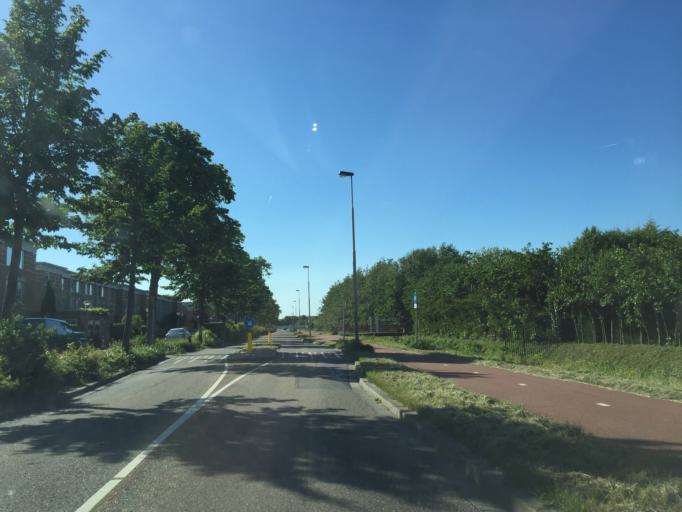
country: NL
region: South Holland
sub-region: Gemeente Lansingerland
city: Bergschenhoek
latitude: 51.9978
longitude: 4.5051
